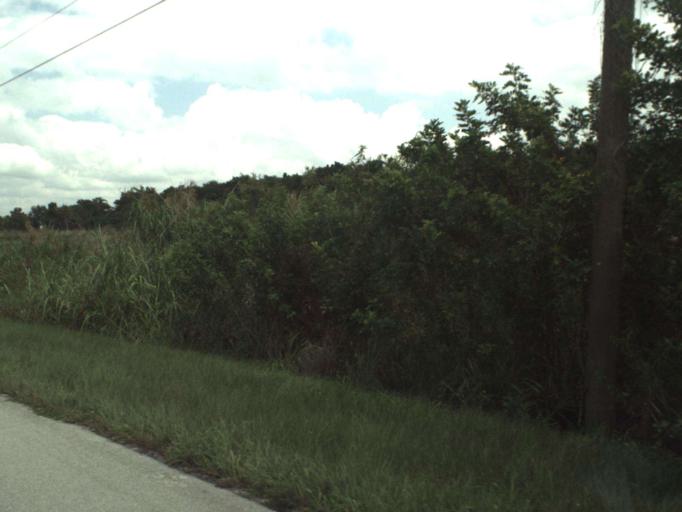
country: US
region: Florida
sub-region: Okeechobee County
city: Taylor Creek
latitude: 27.1205
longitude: -80.6751
